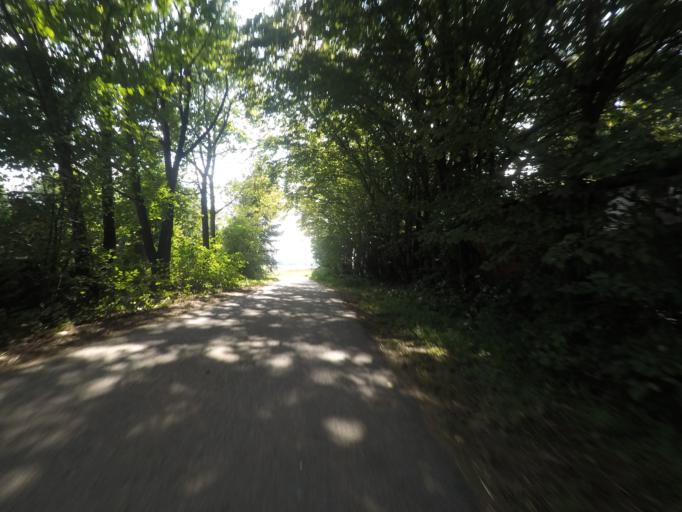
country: DE
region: Baden-Wuerttemberg
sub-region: Regierungsbezirk Stuttgart
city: Schonaich
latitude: 48.6655
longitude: 9.0841
